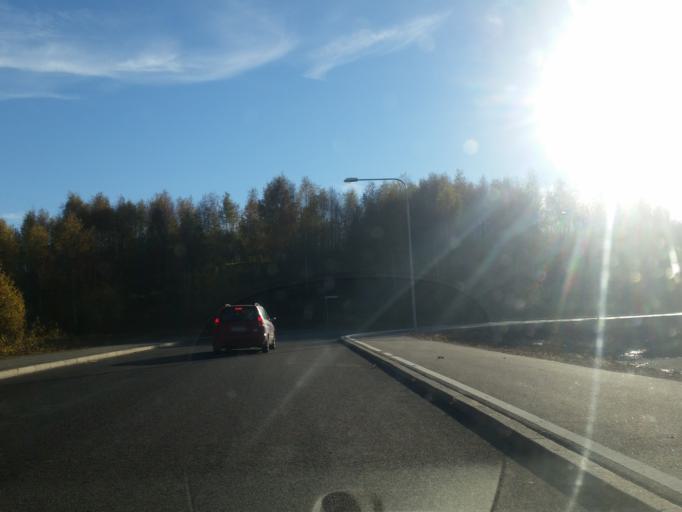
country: SE
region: Dalarna
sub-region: Faluns Kommun
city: Falun
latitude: 60.5967
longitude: 15.6255
